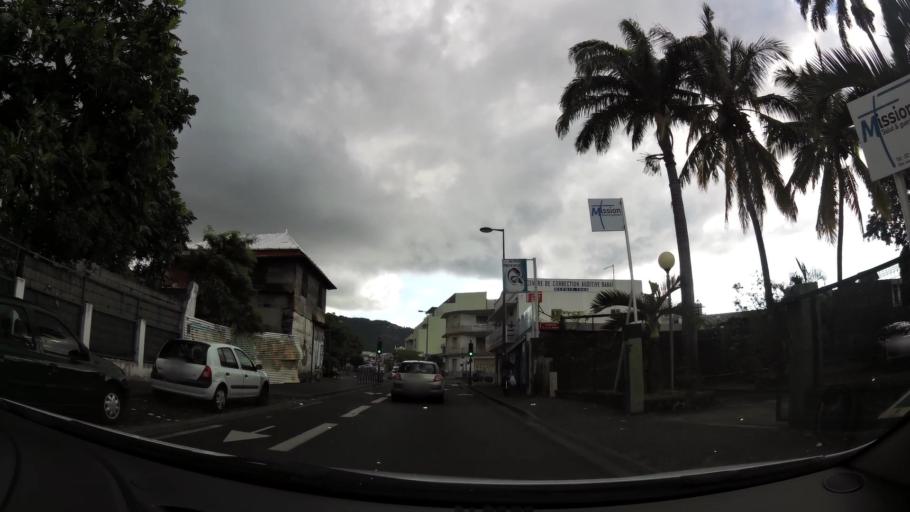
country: RE
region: Reunion
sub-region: Reunion
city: Saint-Denis
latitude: -20.8849
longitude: 55.4614
